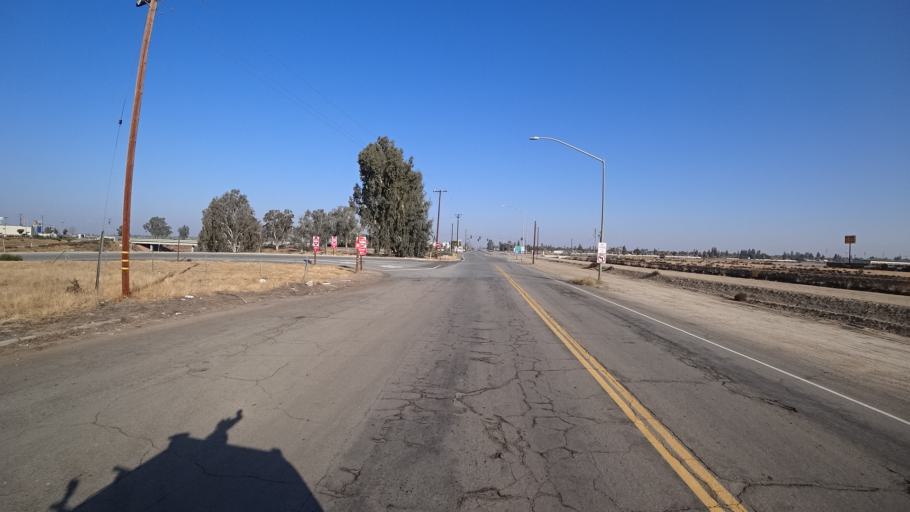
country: US
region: California
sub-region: Kern County
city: Greenfield
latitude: 35.2654
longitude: -119.0214
